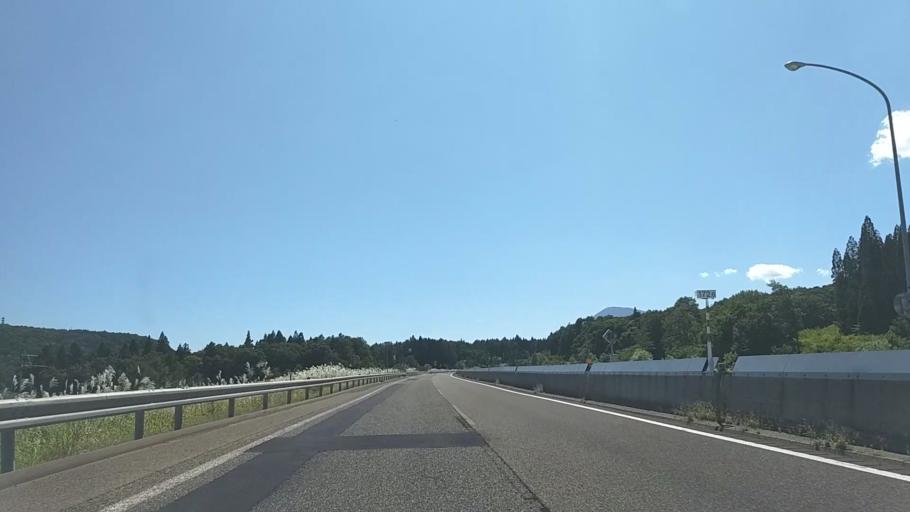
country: JP
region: Niigata
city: Arai
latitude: 36.8678
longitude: 138.1947
